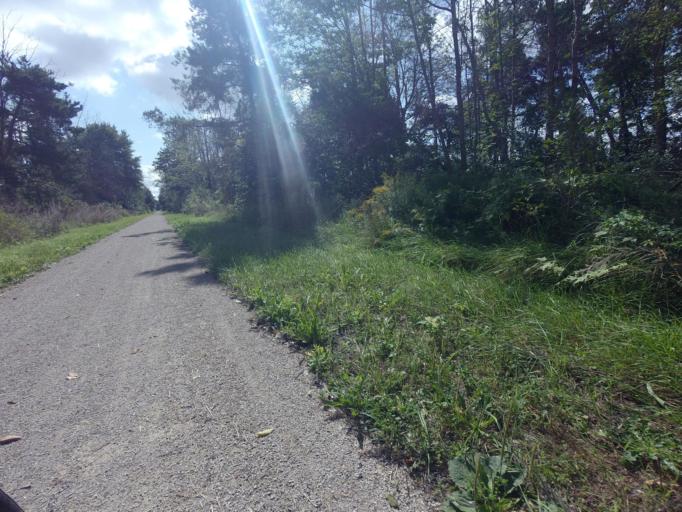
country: CA
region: Ontario
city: Huron East
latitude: 43.6830
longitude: -81.3061
